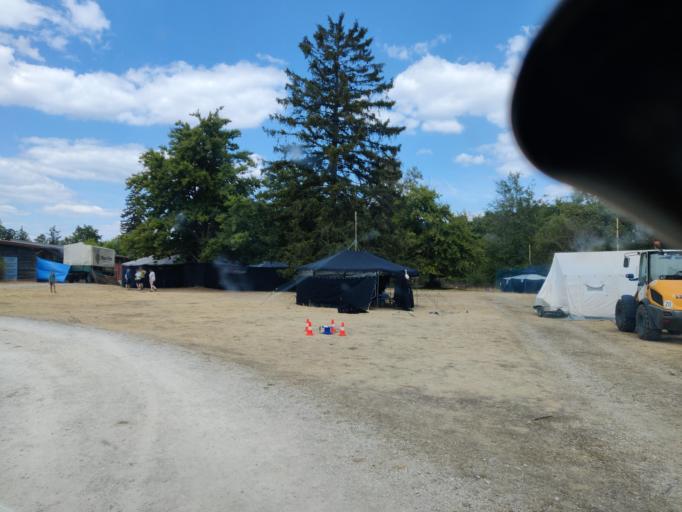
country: DE
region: Bavaria
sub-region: Regierungsbezirk Mittelfranken
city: Thalmassing
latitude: 49.0812
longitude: 11.1876
